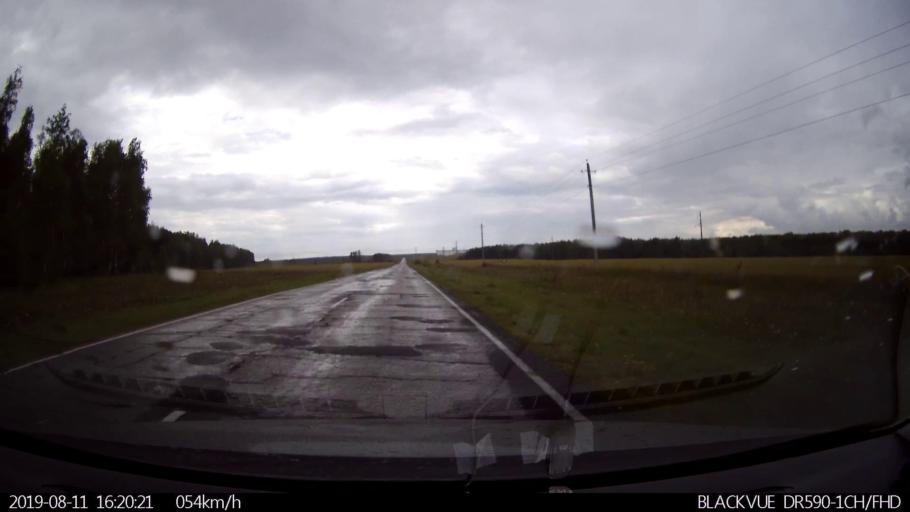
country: RU
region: Ulyanovsk
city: Mayna
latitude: 54.0711
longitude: 47.6033
